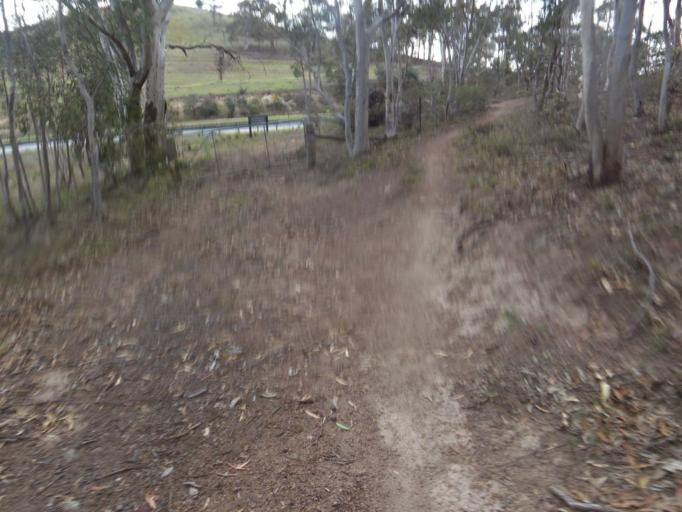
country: AU
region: Australian Capital Territory
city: Forrest
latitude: -35.3484
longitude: 149.1245
